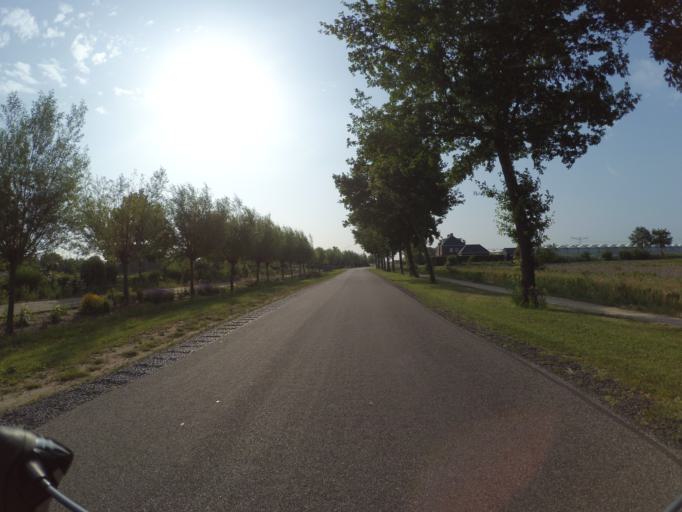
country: NL
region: North Brabant
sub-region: Gemeente Dongen
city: Dongen
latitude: 51.6264
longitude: 4.9801
